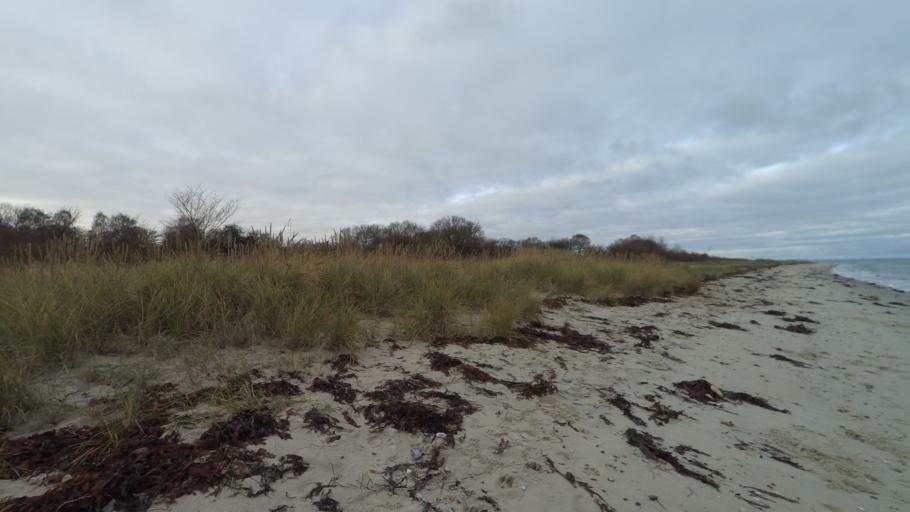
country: DK
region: Central Jutland
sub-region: Arhus Kommune
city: Beder
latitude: 56.0442
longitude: 10.2709
